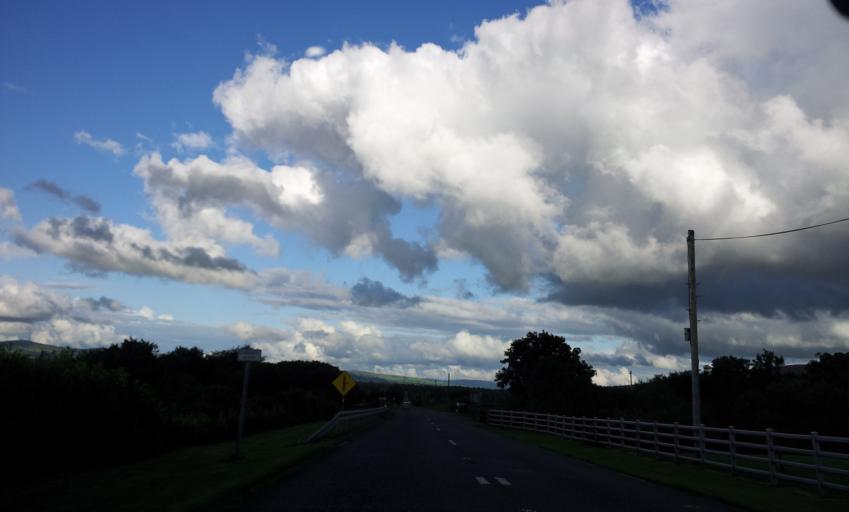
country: IE
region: Munster
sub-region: Ciarrai
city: Tralee
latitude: 52.2439
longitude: -9.7790
